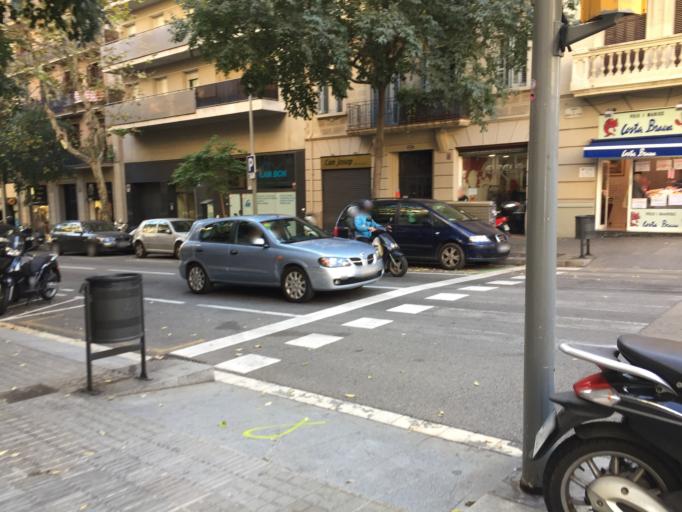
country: ES
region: Catalonia
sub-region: Provincia de Barcelona
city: Gracia
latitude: 41.4028
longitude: 2.1678
